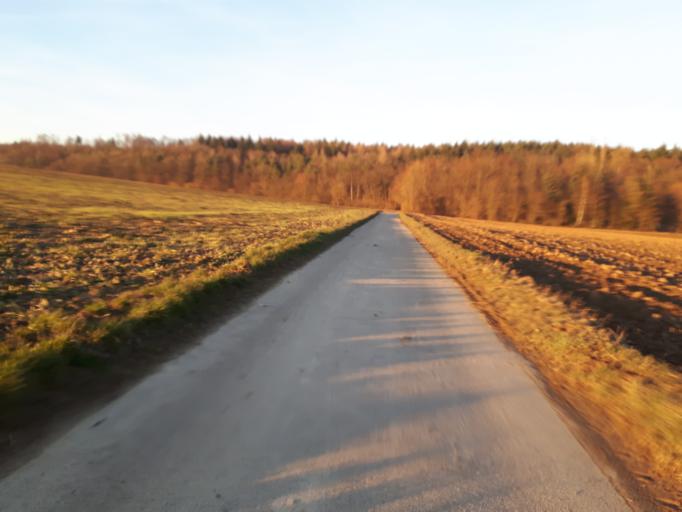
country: DE
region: Baden-Wuerttemberg
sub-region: Regierungsbezirk Stuttgart
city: Massenbachhausen
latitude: 49.1832
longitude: 9.0536
